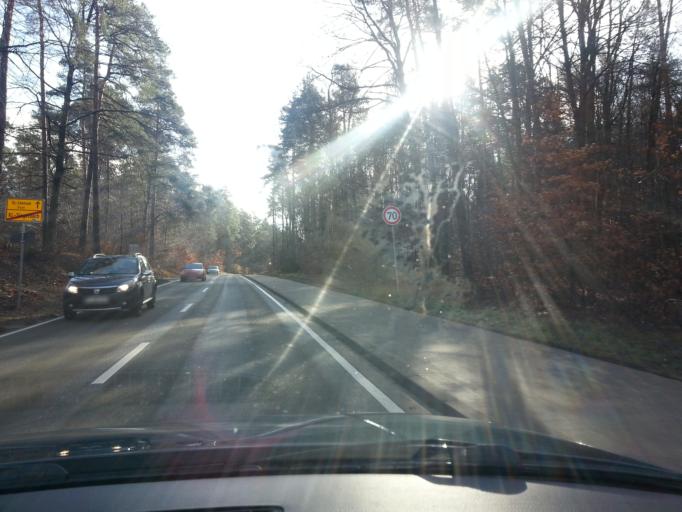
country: DE
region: Rheinland-Pfalz
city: Katzweiler
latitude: 49.4615
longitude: 7.6948
